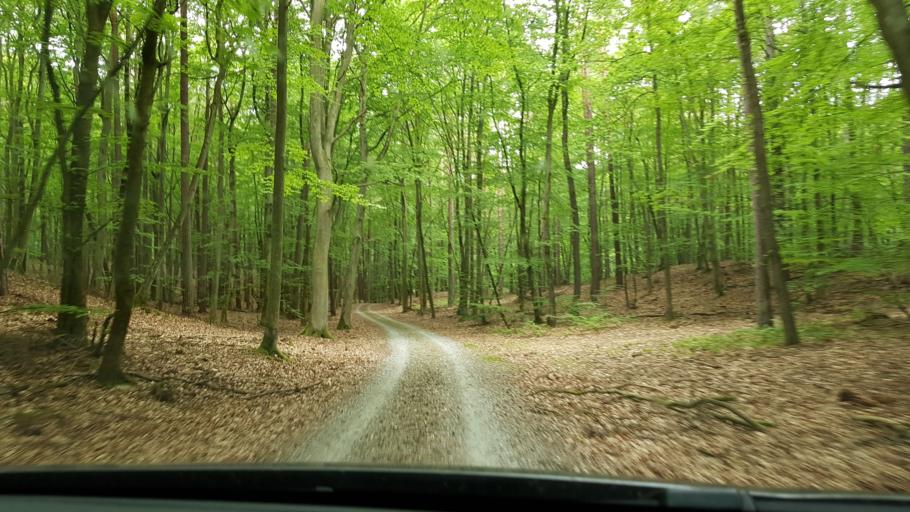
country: PL
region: West Pomeranian Voivodeship
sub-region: Powiat kamienski
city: Miedzyzdroje
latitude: 53.9421
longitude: 14.4860
